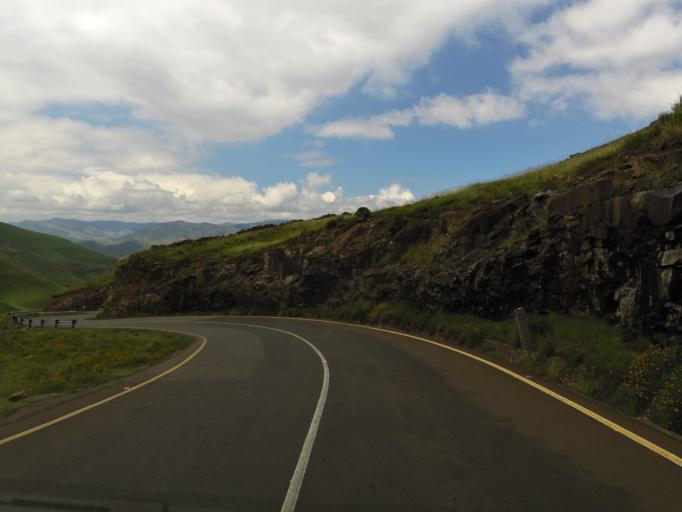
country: LS
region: Butha-Buthe
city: Butha-Buthe
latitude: -29.1123
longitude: 28.4526
